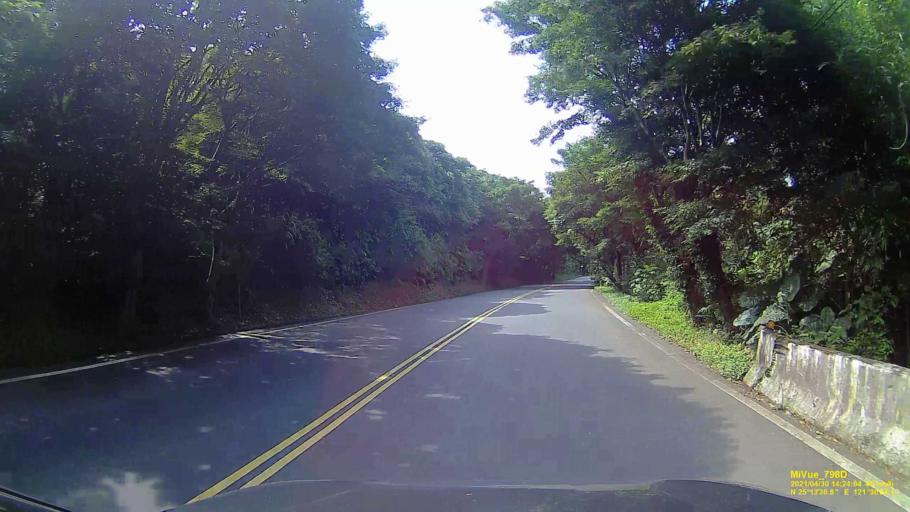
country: TW
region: Taipei
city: Taipei
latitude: 25.2271
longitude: 121.5149
